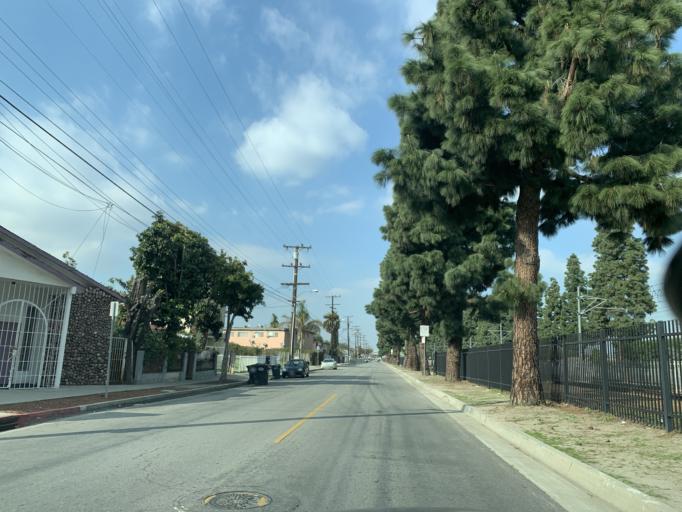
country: US
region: California
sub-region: Los Angeles County
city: Willowbrook
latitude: 33.9208
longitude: -118.2341
